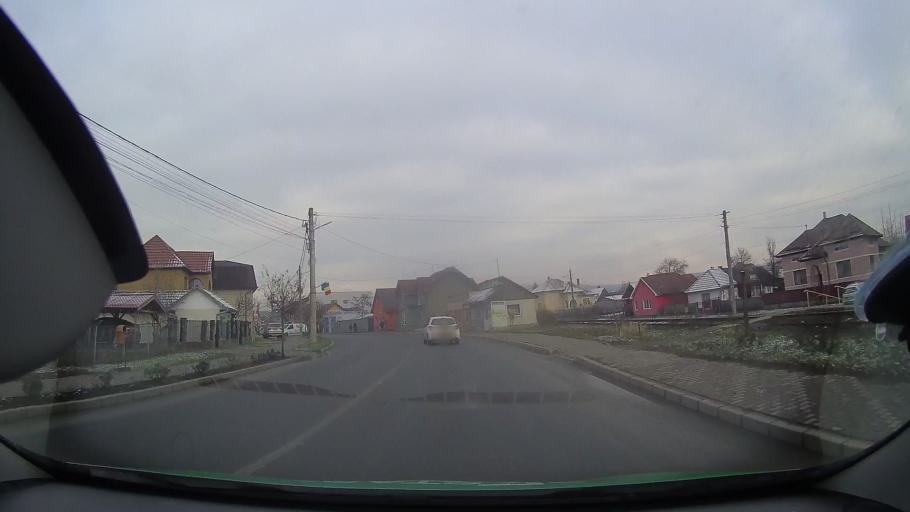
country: RO
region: Mures
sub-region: Comuna Ludus
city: Ludus
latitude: 46.4699
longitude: 24.0950
